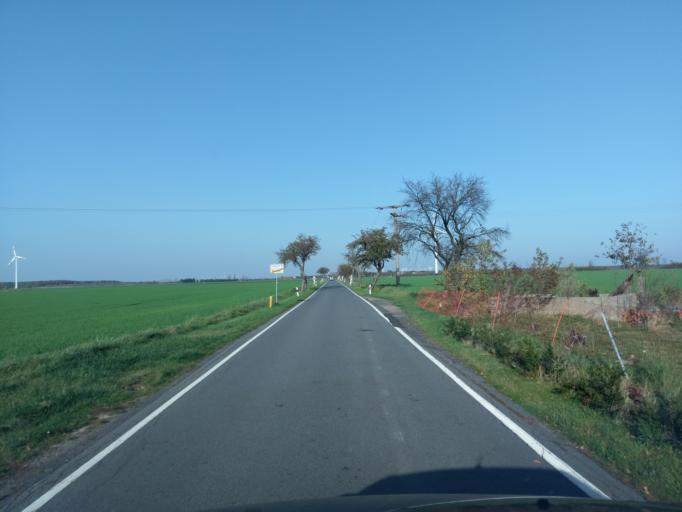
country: DE
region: Brandenburg
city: Muhlberg
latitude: 51.4617
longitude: 13.2579
